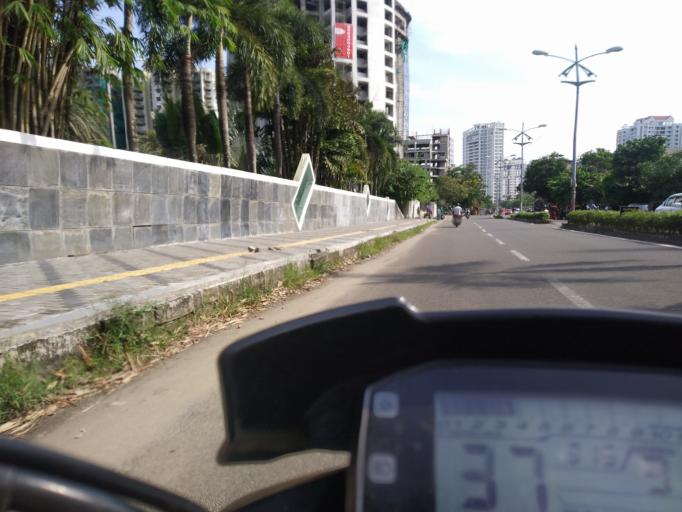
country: IN
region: Kerala
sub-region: Ernakulam
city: Cochin
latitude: 9.9910
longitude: 76.3021
